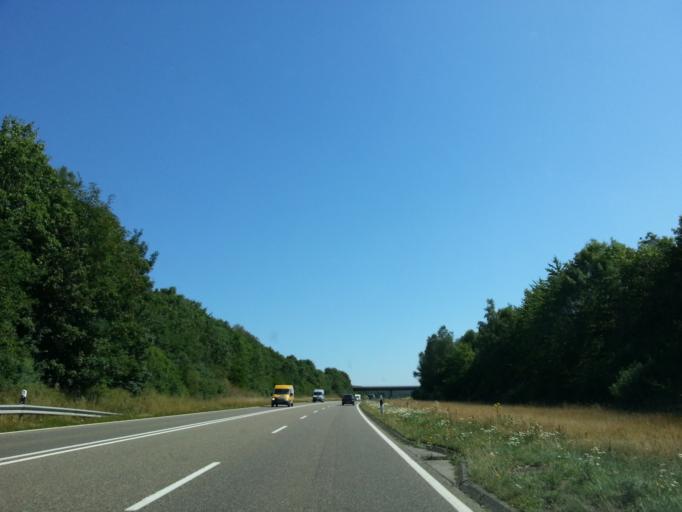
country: DE
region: Rheinland-Pfalz
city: Brandscheid
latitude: 50.2057
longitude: 6.2948
